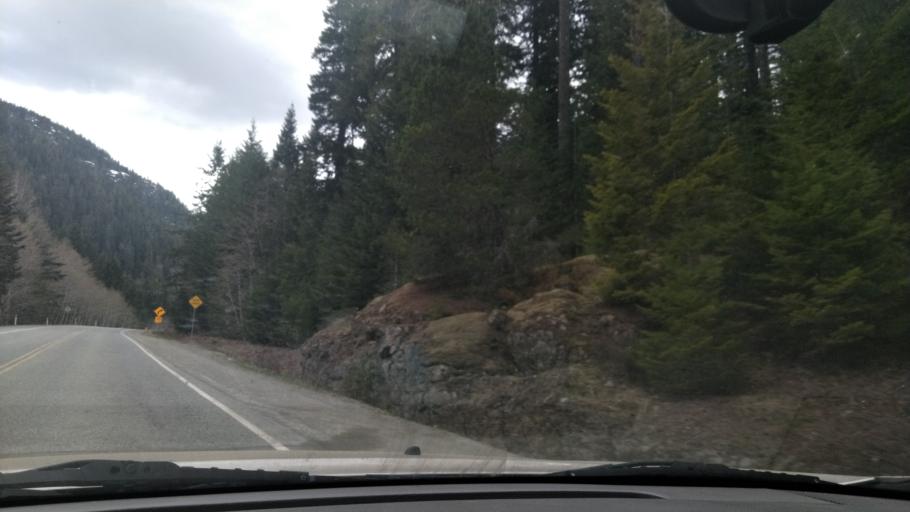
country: CA
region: British Columbia
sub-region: Regional District of Alberni-Clayoquot
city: Tofino
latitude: 49.8409
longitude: -125.9174
